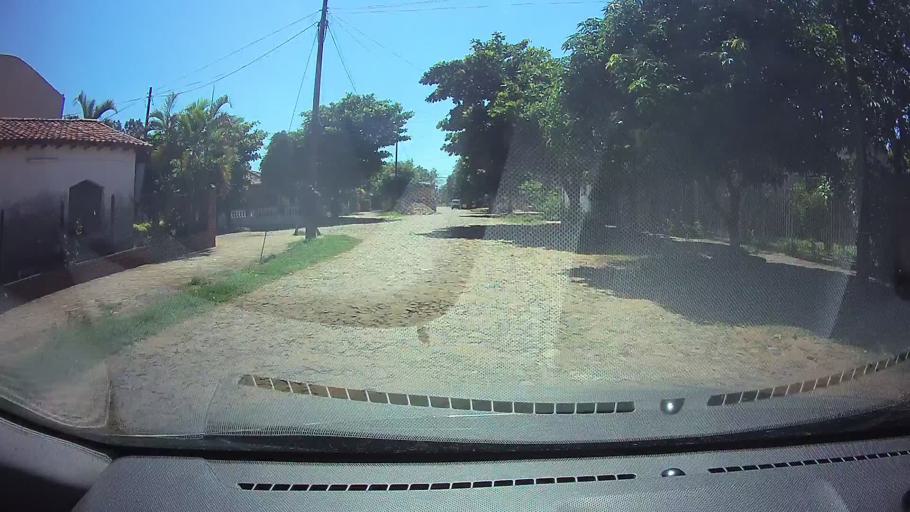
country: PY
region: Central
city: Fernando de la Mora
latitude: -25.3035
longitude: -57.5289
